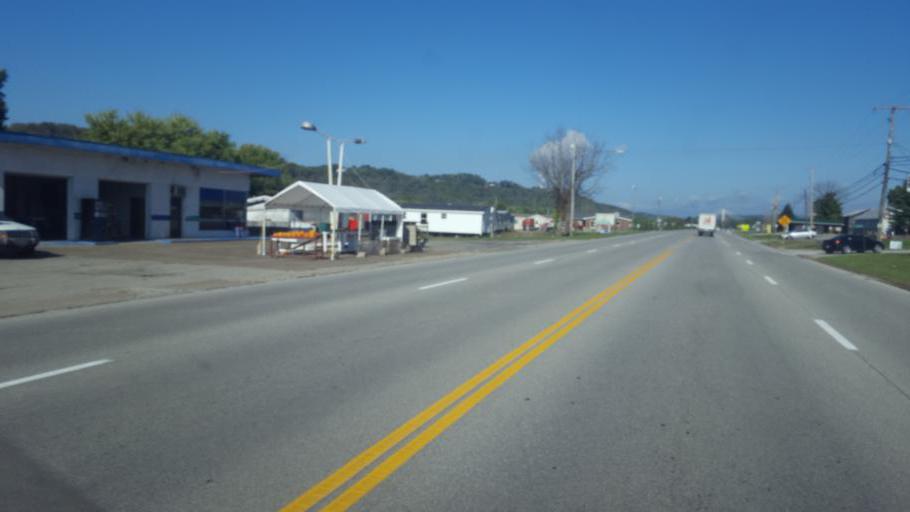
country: US
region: Ohio
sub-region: Brown County
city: Aberdeen
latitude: 38.6610
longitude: -83.7675
